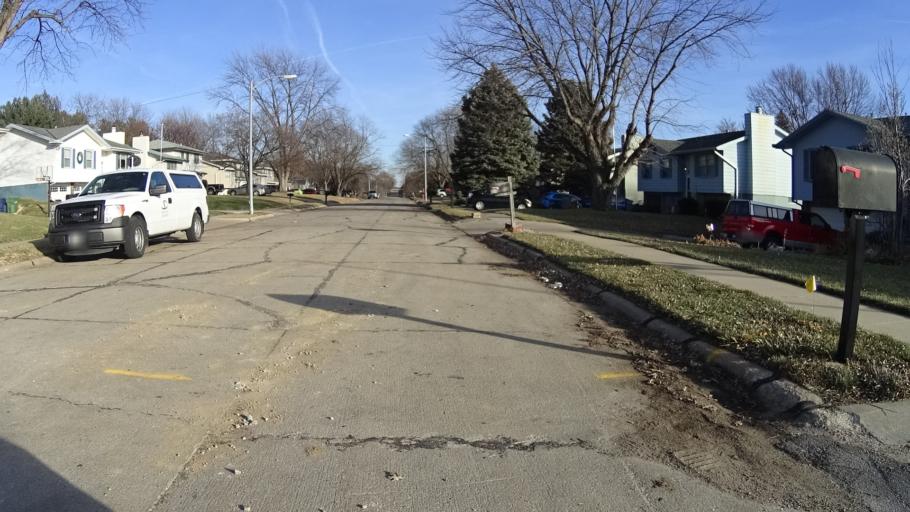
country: US
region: Nebraska
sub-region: Sarpy County
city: Offutt Air Force Base
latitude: 41.1764
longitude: -95.9510
